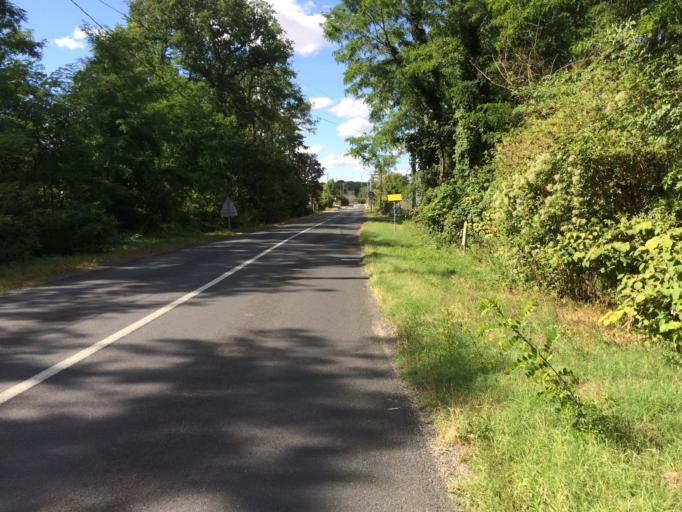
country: FR
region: Ile-de-France
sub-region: Departement de l'Essonne
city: Cerny
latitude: 48.4517
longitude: 2.3423
